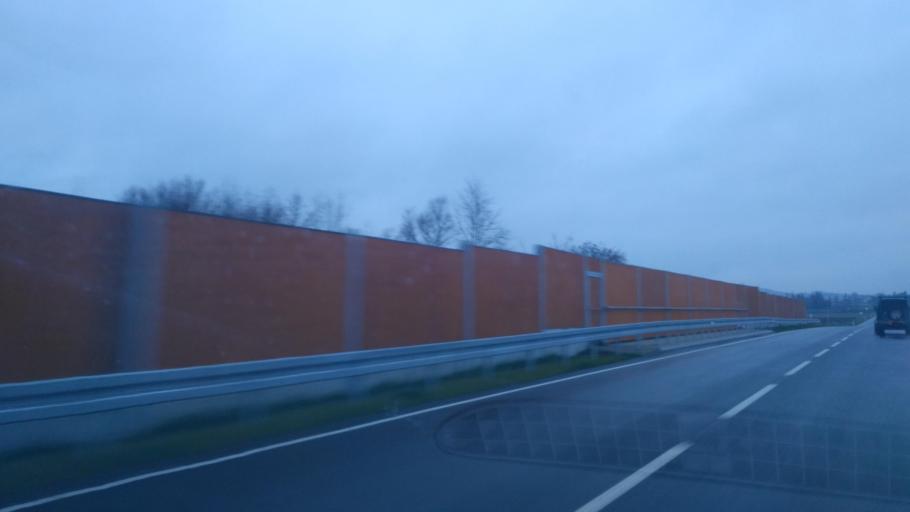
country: PL
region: Subcarpathian Voivodeship
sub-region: Powiat rzeszowski
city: Dynow
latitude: 49.8274
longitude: 22.2416
